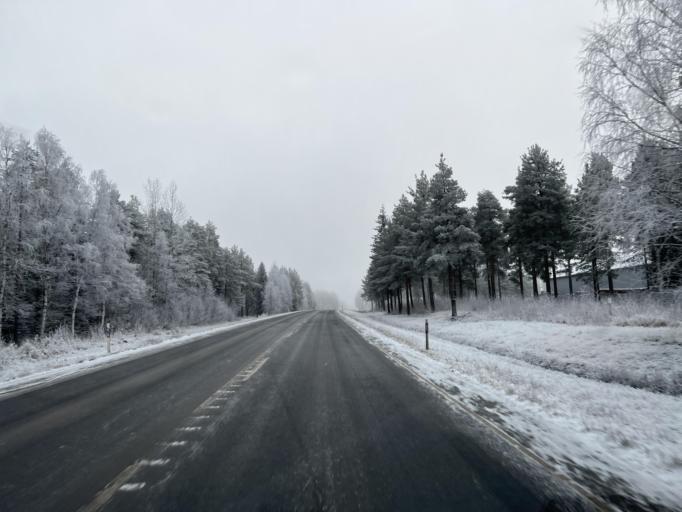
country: FI
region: Northern Ostrobothnia
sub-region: Oulunkaari
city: Utajaervi
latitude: 64.7398
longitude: 26.4587
